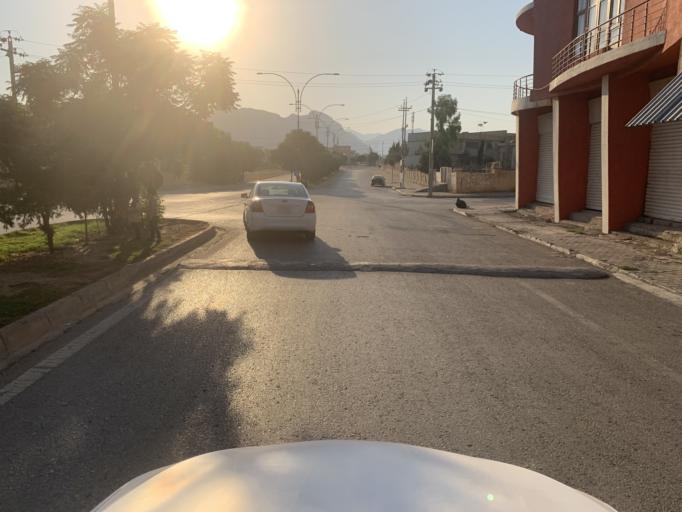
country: IQ
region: As Sulaymaniyah
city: Raniye
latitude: 36.2396
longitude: 44.8775
